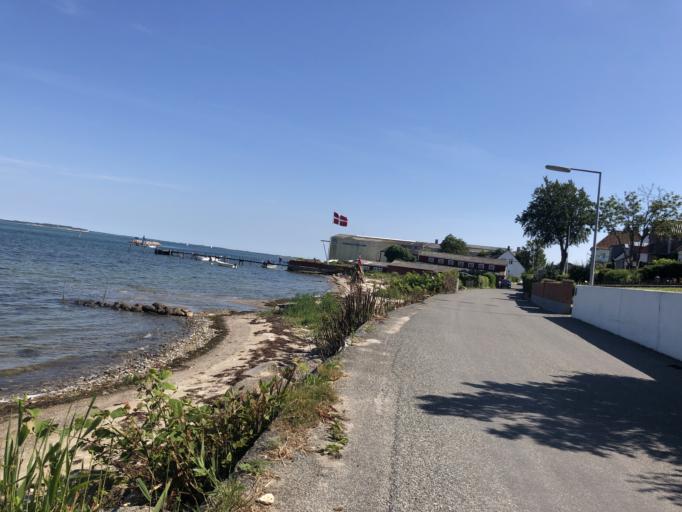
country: DK
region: South Denmark
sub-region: AEro Kommune
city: Marstal
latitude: 54.8594
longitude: 10.5190
